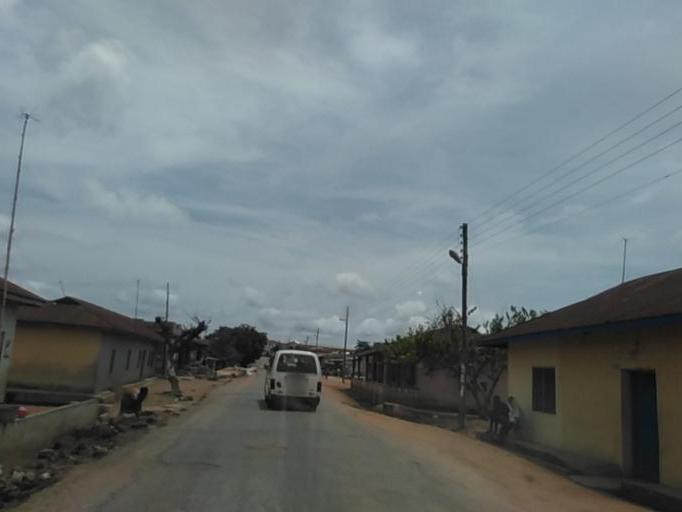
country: GH
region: Ashanti
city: Mamponteng
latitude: 6.8261
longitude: -1.4953
